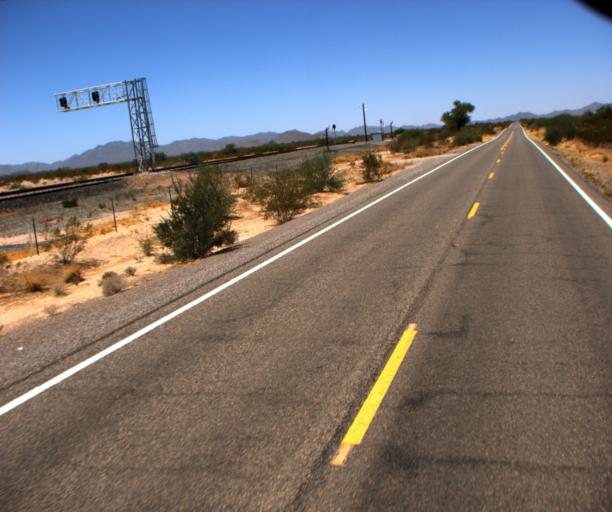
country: US
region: Arizona
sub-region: Pinal County
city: Maricopa
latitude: 33.0472
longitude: -112.3043
